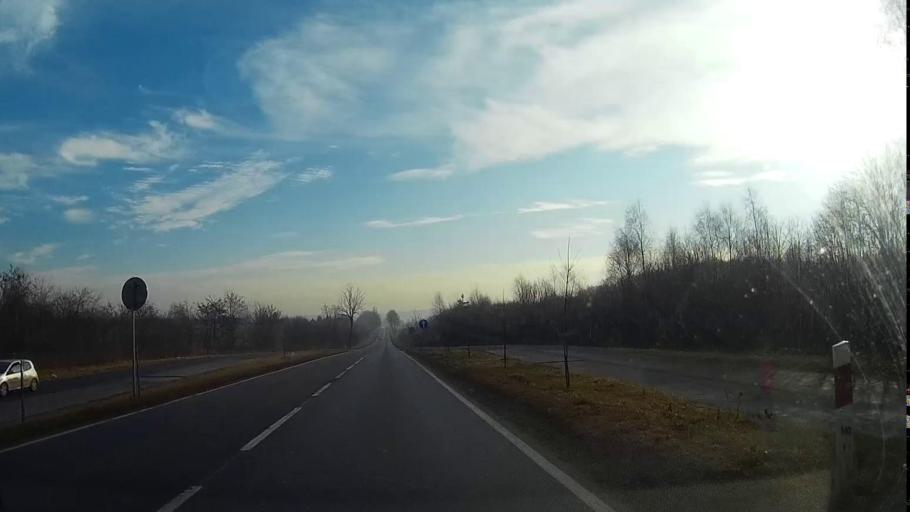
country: PL
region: Lesser Poland Voivodeship
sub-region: Powiat chrzanowski
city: Kwaczala
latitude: 50.0604
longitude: 19.5102
